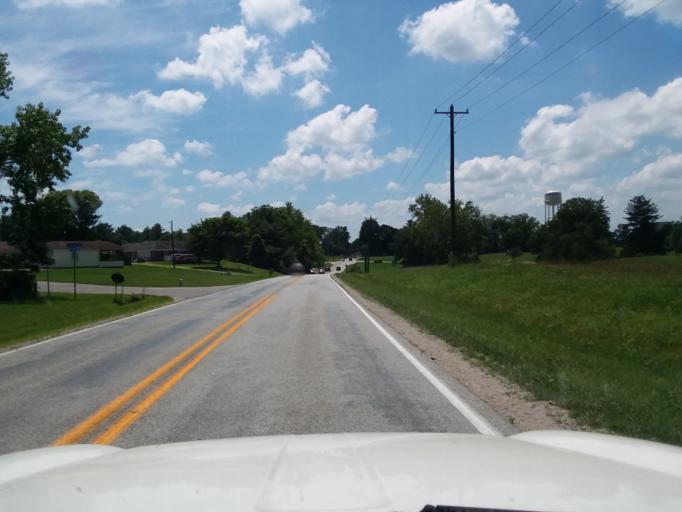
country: US
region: Indiana
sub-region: Johnson County
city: Trafalgar
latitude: 39.3741
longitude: -86.2525
